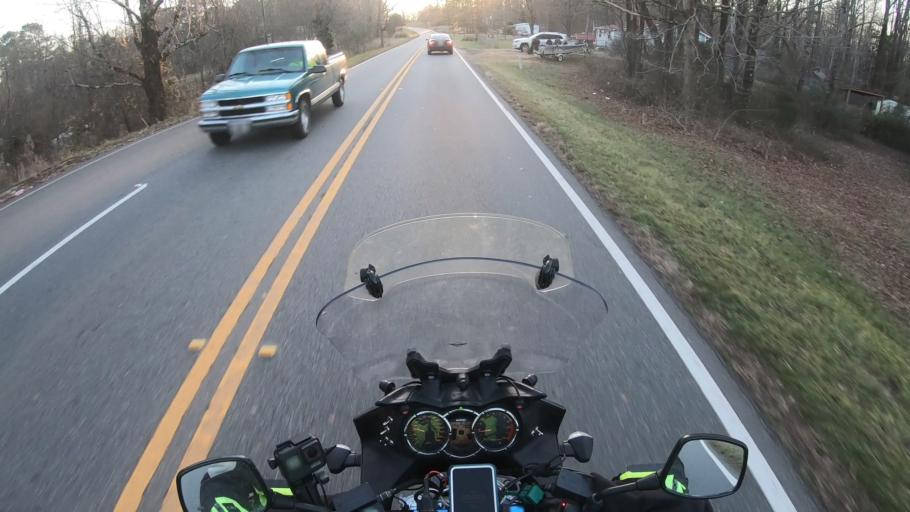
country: US
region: Georgia
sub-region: Dawson County
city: Dawsonville
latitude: 34.3266
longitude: -84.1322
